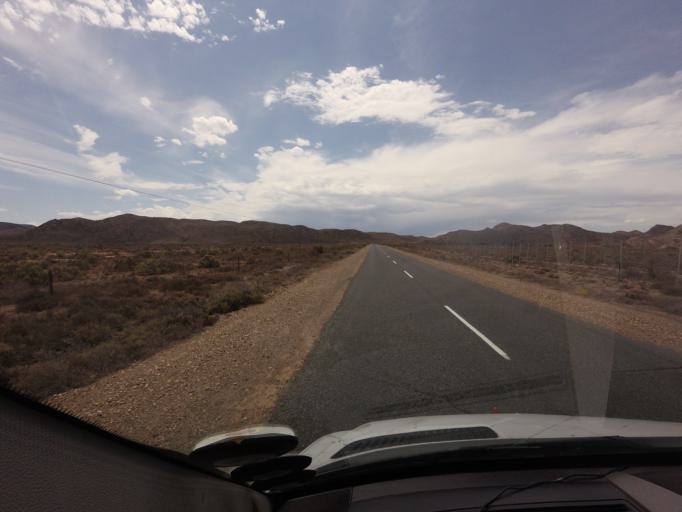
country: ZA
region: Western Cape
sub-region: Eden District Municipality
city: Ladismith
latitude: -33.7263
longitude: 20.9589
